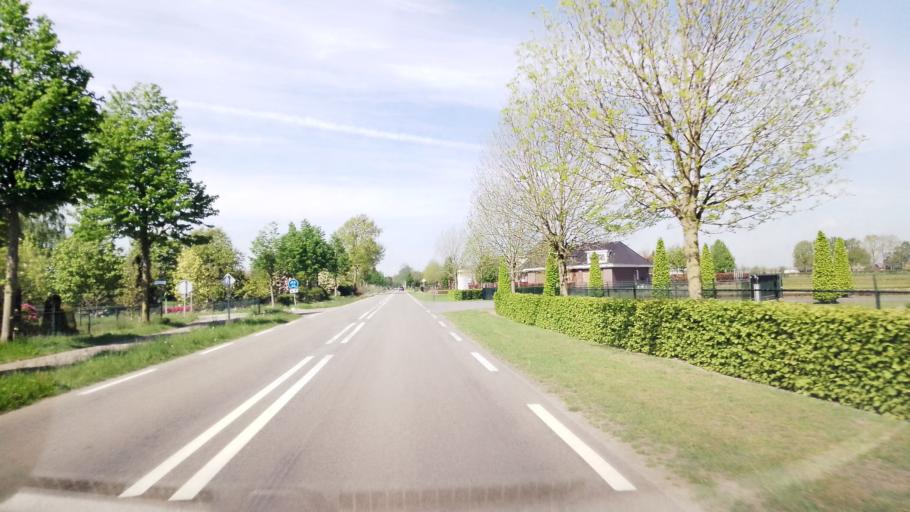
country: NL
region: Limburg
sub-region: Gemeente Venlo
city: Arcen
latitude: 51.4557
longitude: 6.1084
